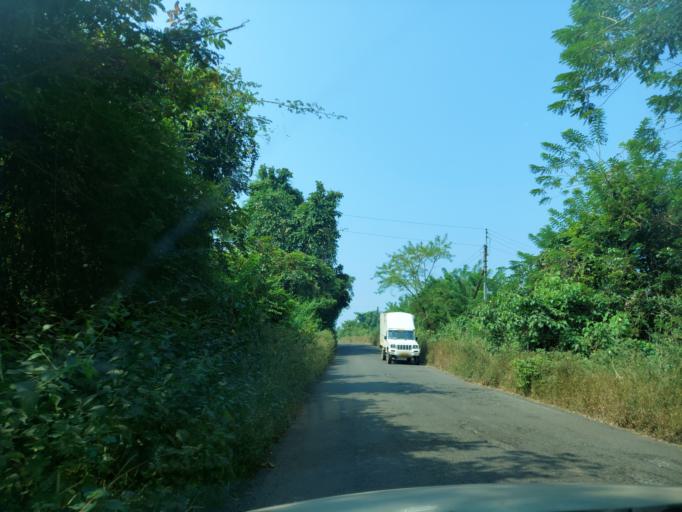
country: IN
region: Maharashtra
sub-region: Sindhudurg
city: Kudal
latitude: 15.9791
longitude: 73.6597
